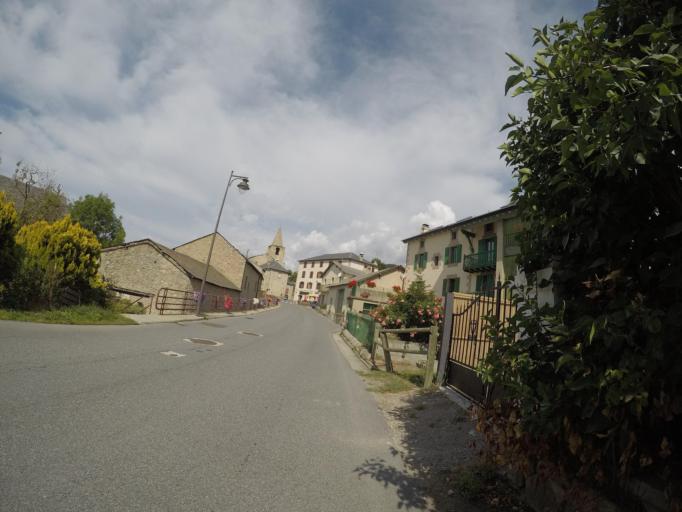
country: ES
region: Catalonia
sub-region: Provincia de Girona
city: Llivia
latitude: 42.4974
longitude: 2.0351
